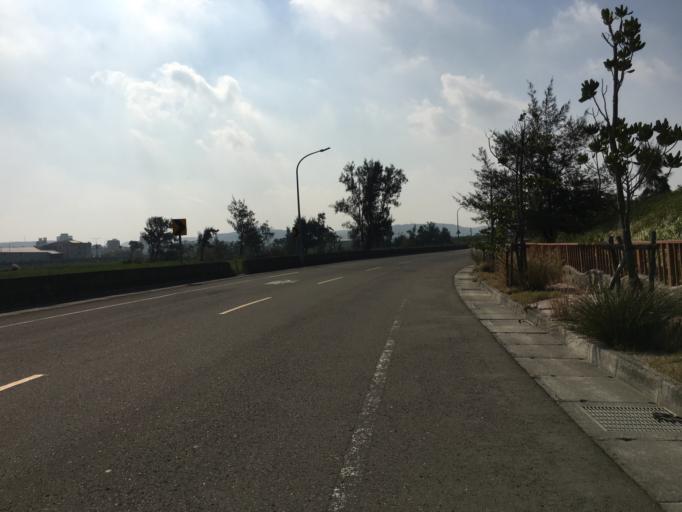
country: TW
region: Taiwan
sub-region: Hsinchu
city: Hsinchu
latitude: 24.7985
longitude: 120.9174
